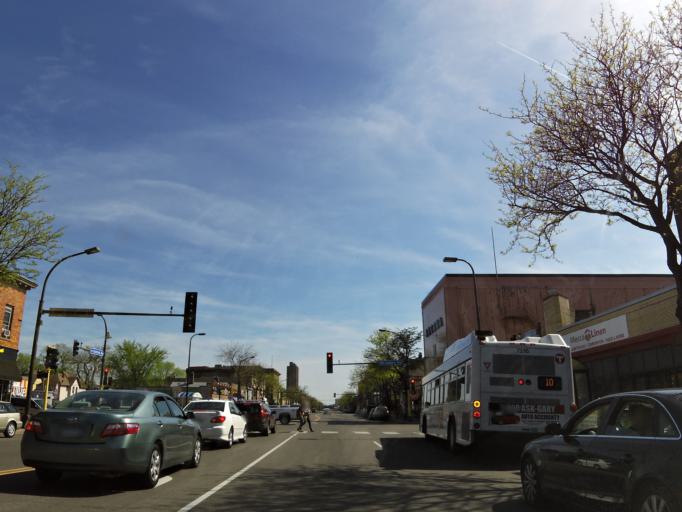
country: US
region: Minnesota
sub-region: Hennepin County
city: Saint Anthony
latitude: 45.0135
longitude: -93.2474
